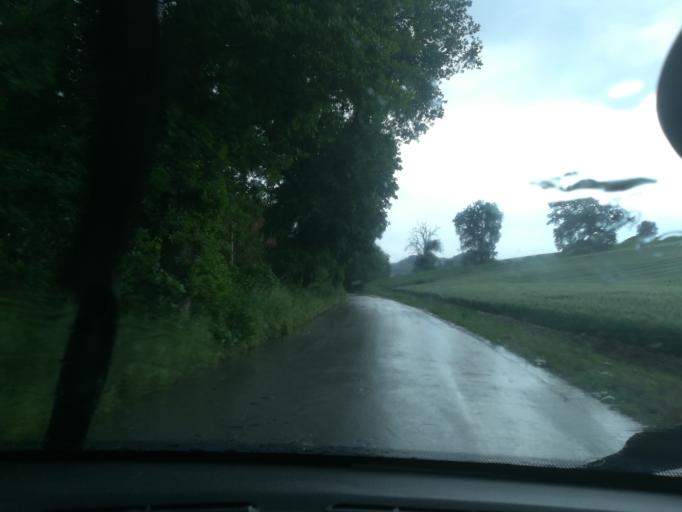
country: IT
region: The Marches
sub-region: Provincia di Macerata
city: Passo di Treia
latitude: 43.2985
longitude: 13.3457
